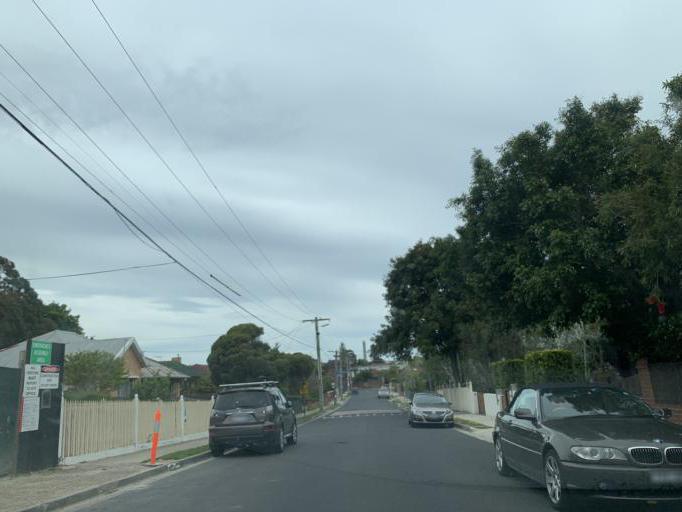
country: AU
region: Victoria
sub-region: Bayside
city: Highett
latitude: -37.9468
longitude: 145.0389
